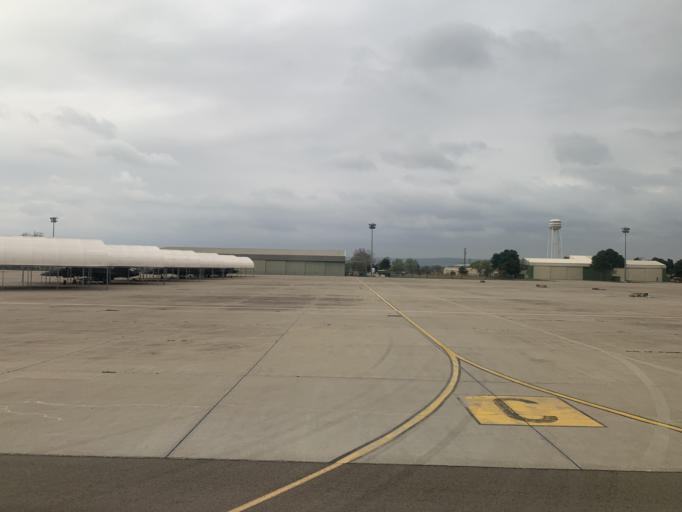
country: ES
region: Aragon
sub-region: Provincia de Zaragoza
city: Utebo
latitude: 41.6667
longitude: -1.0277
